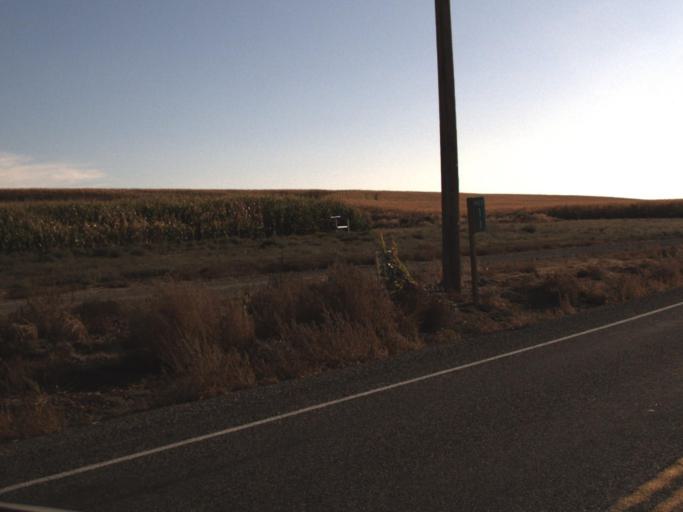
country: US
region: Washington
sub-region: Walla Walla County
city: Burbank
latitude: 46.2526
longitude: -118.8058
